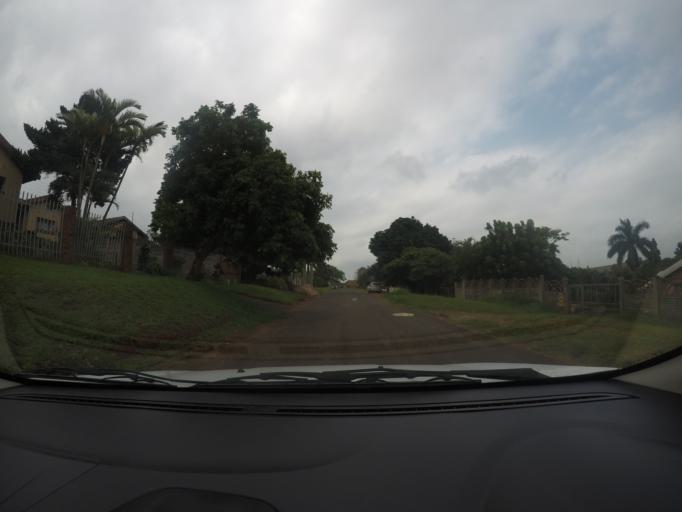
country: ZA
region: KwaZulu-Natal
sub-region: uThungulu District Municipality
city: Empangeni
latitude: -28.7375
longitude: 31.9013
